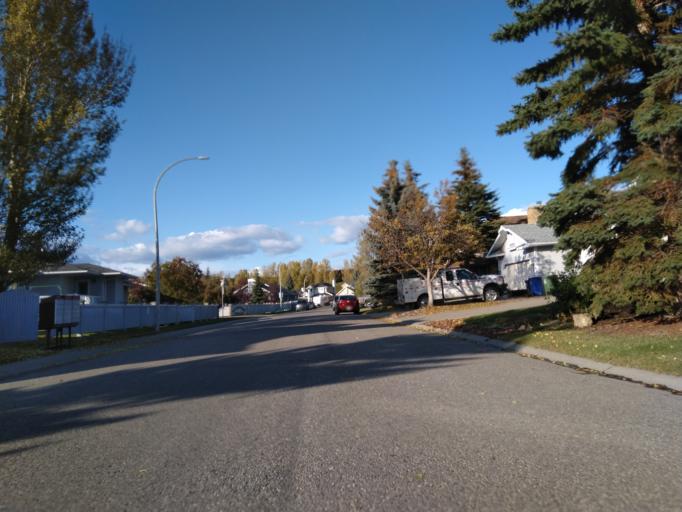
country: CA
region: Alberta
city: Cochrane
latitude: 51.1777
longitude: -114.4759
